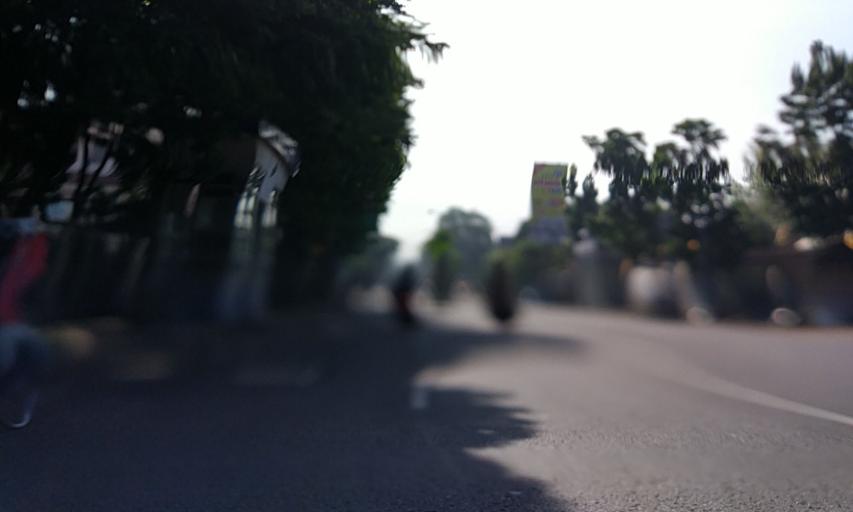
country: ID
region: West Java
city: Bandung
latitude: -6.9164
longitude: 107.6286
